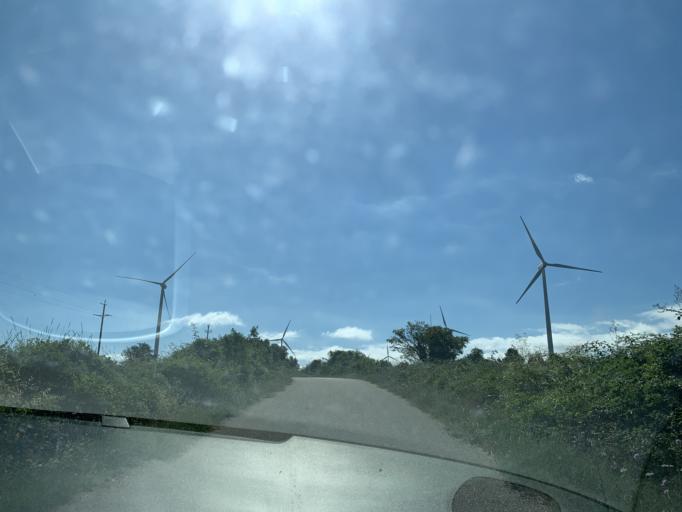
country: ES
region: Catalonia
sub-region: Provincia de Tarragona
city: Conesa
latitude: 41.5425
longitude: 1.2705
